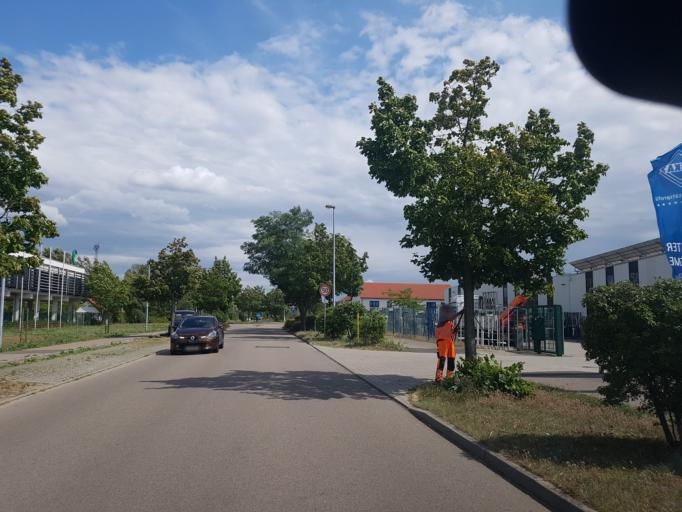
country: DE
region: Brandenburg
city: Herzberg
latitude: 51.6761
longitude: 13.2182
